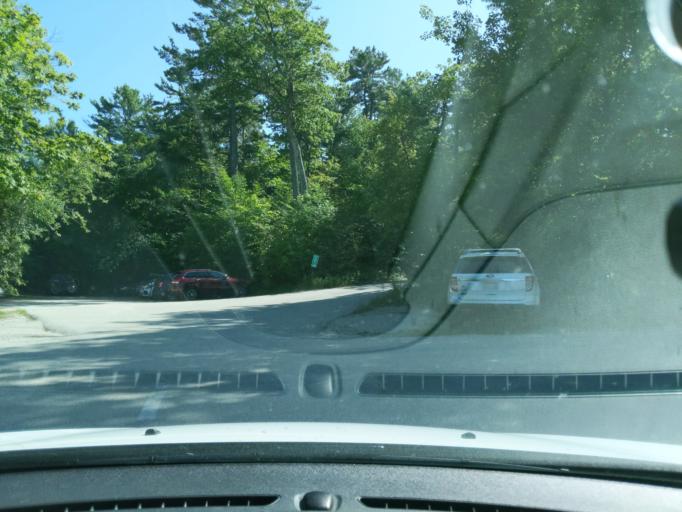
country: US
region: Michigan
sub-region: Delta County
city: Escanaba
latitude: 45.2899
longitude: -86.9776
